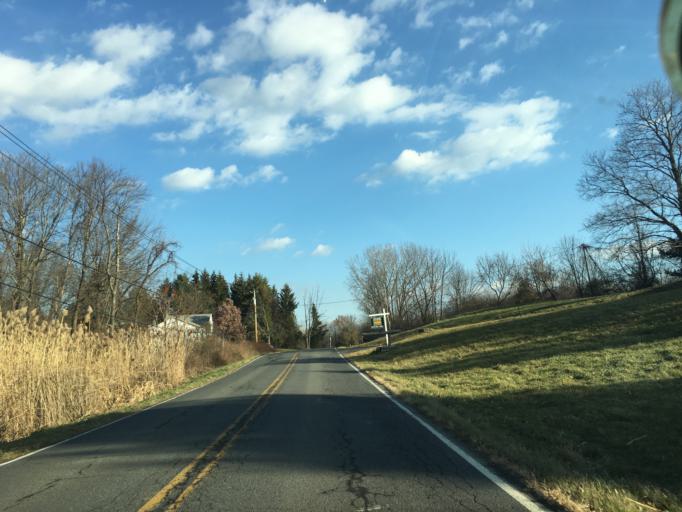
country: US
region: New York
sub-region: Rensselaer County
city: East Greenbush
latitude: 42.6339
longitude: -73.6818
